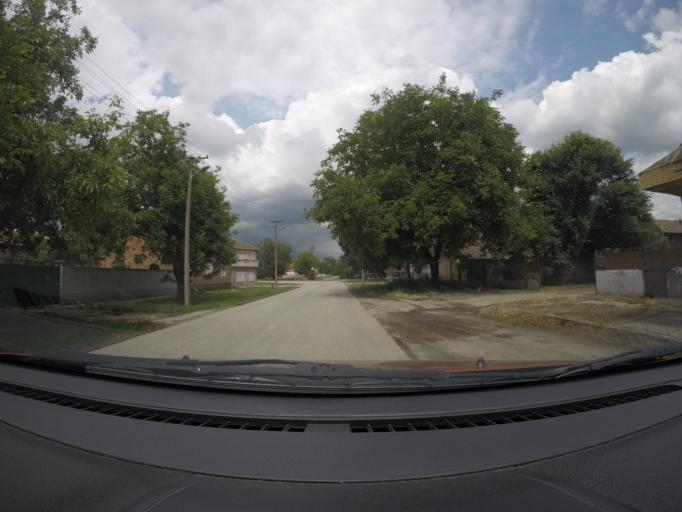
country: RS
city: Centa
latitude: 45.1128
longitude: 20.3898
